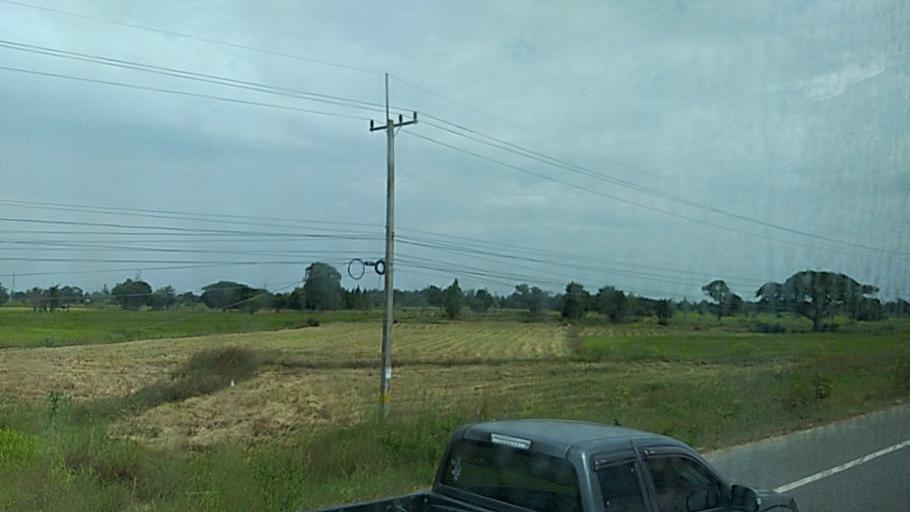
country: TH
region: Roi Et
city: Changhan
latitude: 16.0911
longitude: 103.5489
